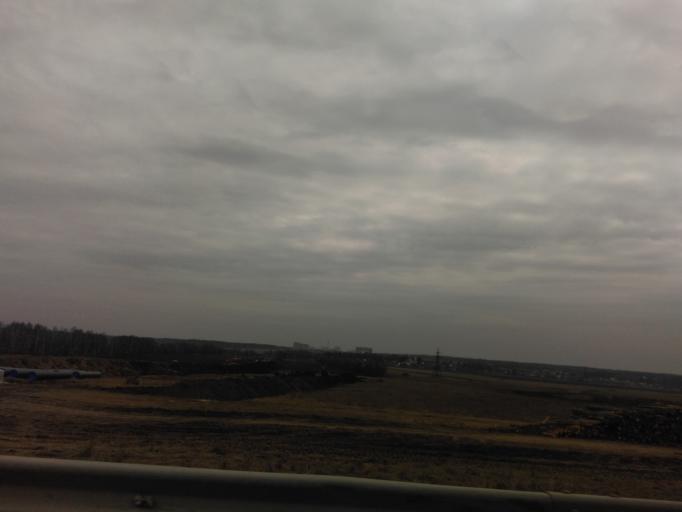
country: RU
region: Moskovskaya
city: Nikolina Gora
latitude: 55.7388
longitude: 36.9968
